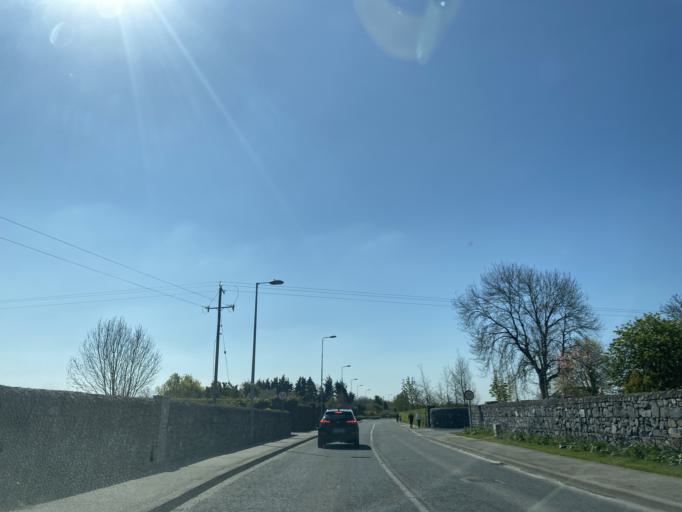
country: IE
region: Leinster
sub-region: Kildare
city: Celbridge
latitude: 53.3200
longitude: -6.6058
